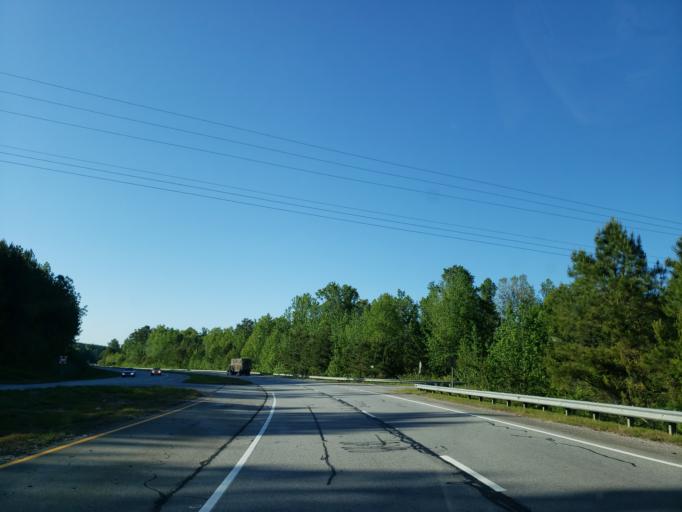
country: US
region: Georgia
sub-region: Haralson County
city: Buchanan
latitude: 33.8458
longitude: -85.2075
